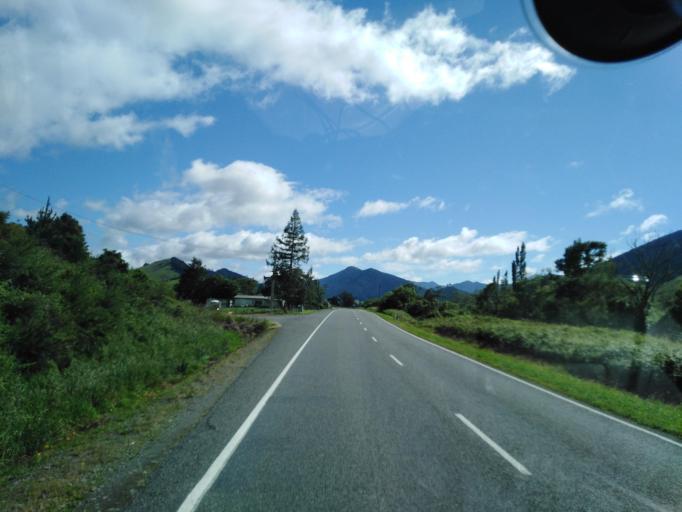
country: NZ
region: Nelson
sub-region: Nelson City
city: Nelson
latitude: -41.2448
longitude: 173.5769
